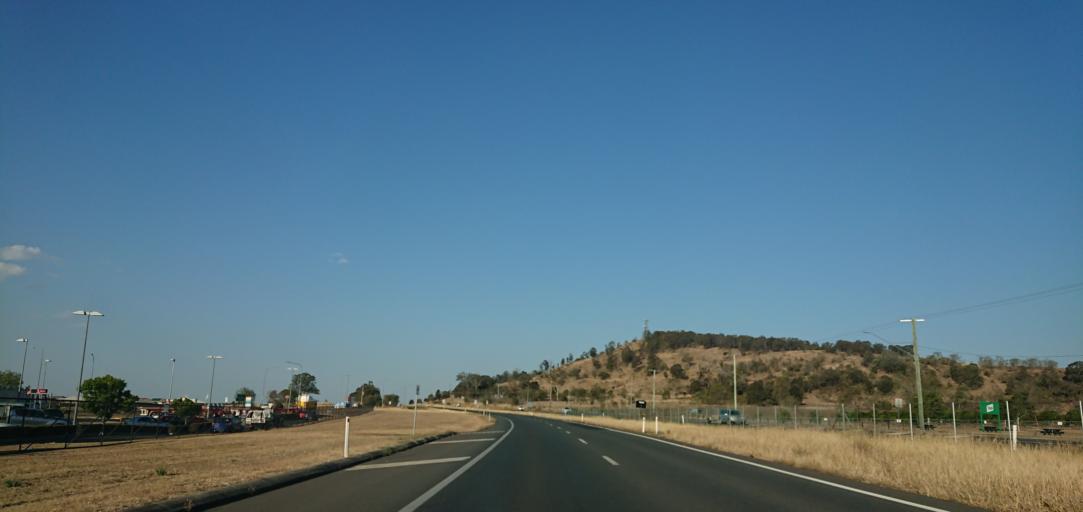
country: AU
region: Queensland
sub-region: Lockyer Valley
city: Gatton
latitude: -27.5655
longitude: 152.4240
